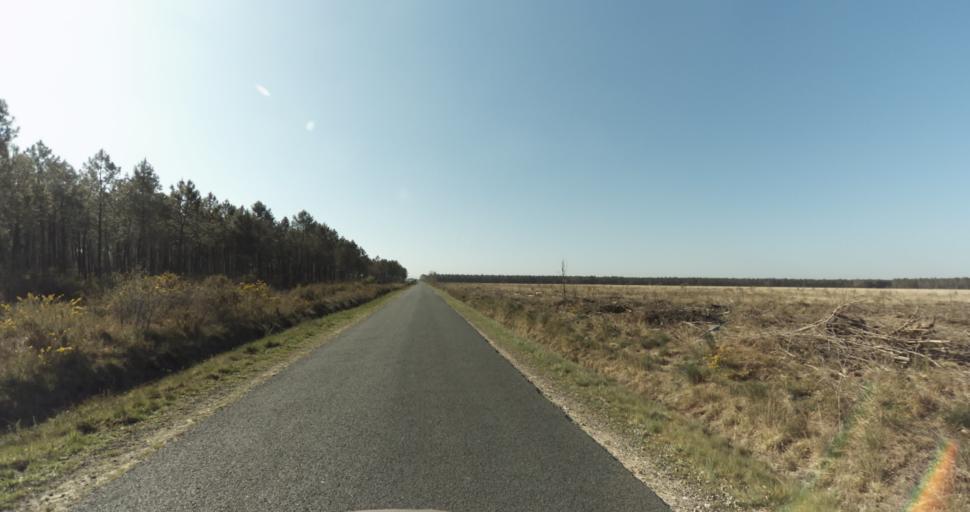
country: FR
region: Aquitaine
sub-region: Departement de la Gironde
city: Marcheprime
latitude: 44.7819
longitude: -0.8611
